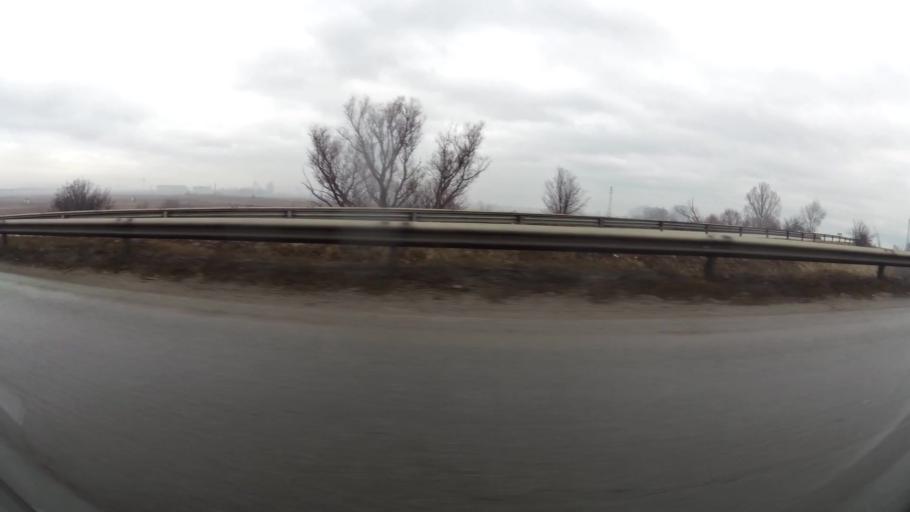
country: BG
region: Sofia-Capital
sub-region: Stolichna Obshtina
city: Sofia
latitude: 42.7091
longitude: 23.4482
